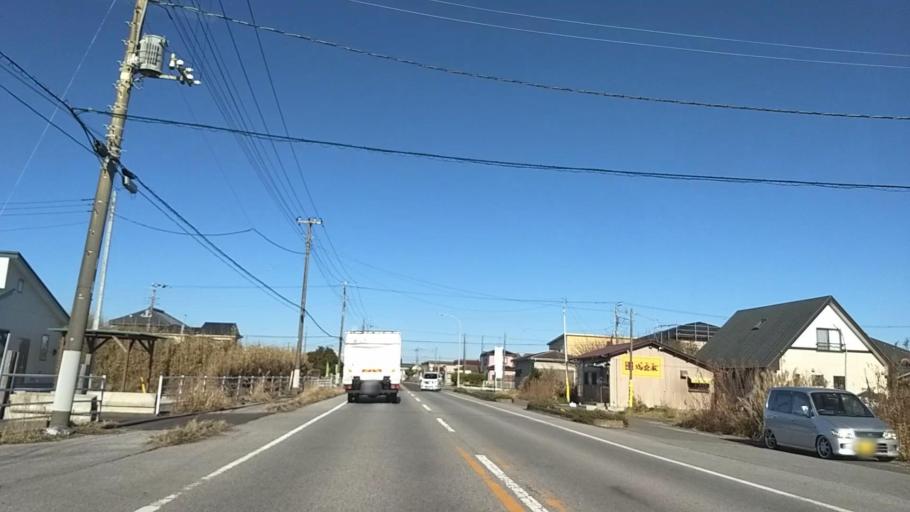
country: JP
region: Chiba
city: Togane
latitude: 35.5220
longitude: 140.4434
